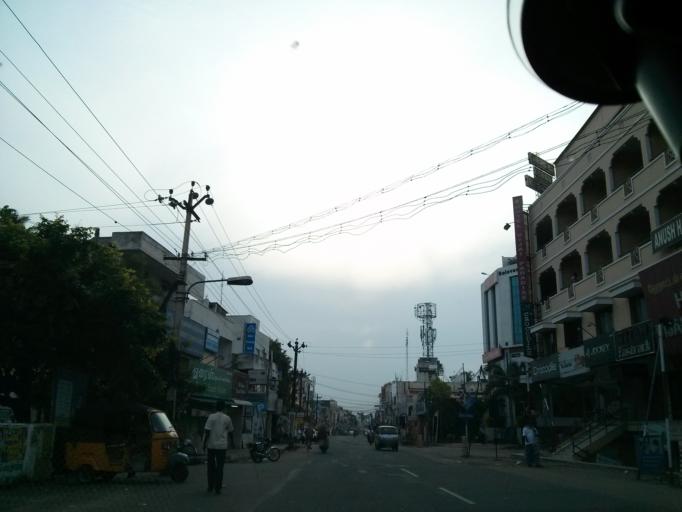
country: IN
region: Tamil Nadu
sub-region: Coimbatore
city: Coimbatore
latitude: 11.0261
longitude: 76.9432
